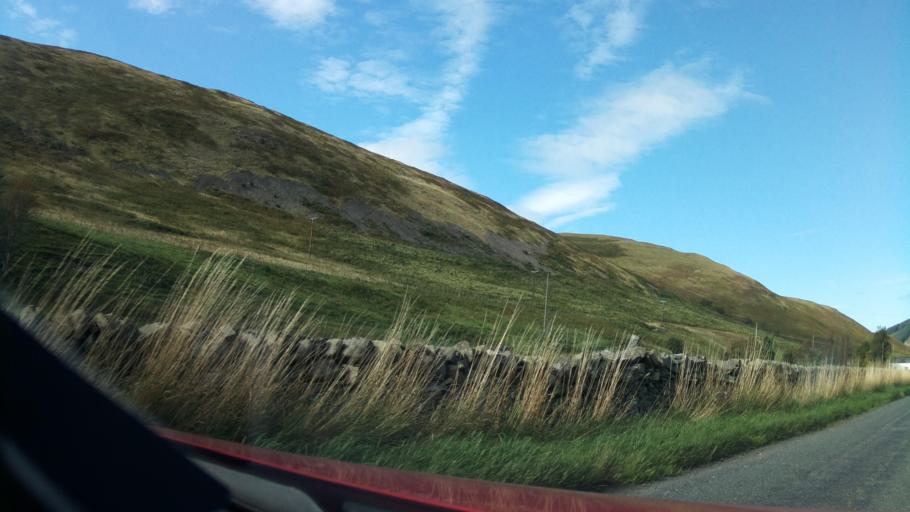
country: GB
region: Scotland
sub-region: South Lanarkshire
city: Biggar
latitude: 55.5191
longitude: -3.4132
